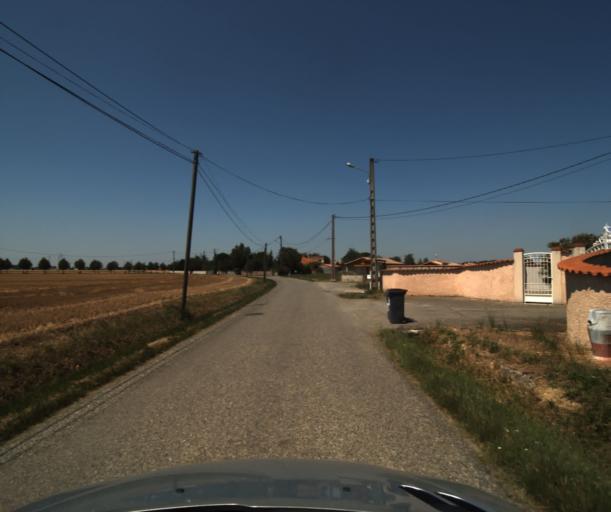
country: FR
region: Midi-Pyrenees
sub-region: Departement de la Haute-Garonne
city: Muret
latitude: 43.4677
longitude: 1.3647
